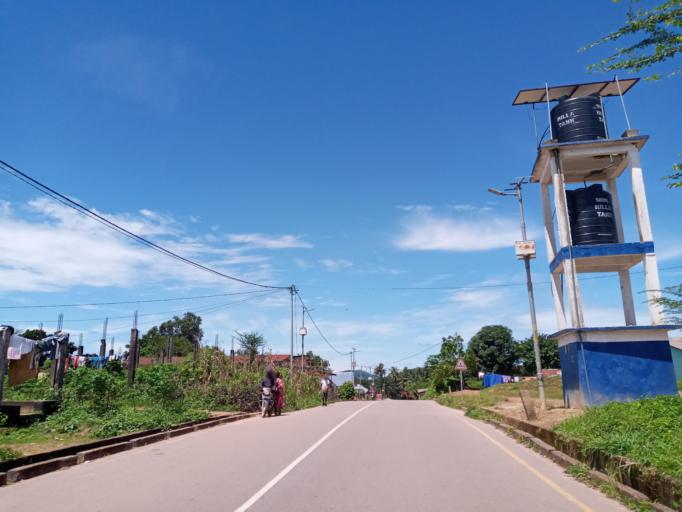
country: SL
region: Eastern Province
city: Koidu
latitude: 8.6470
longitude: -10.9629
